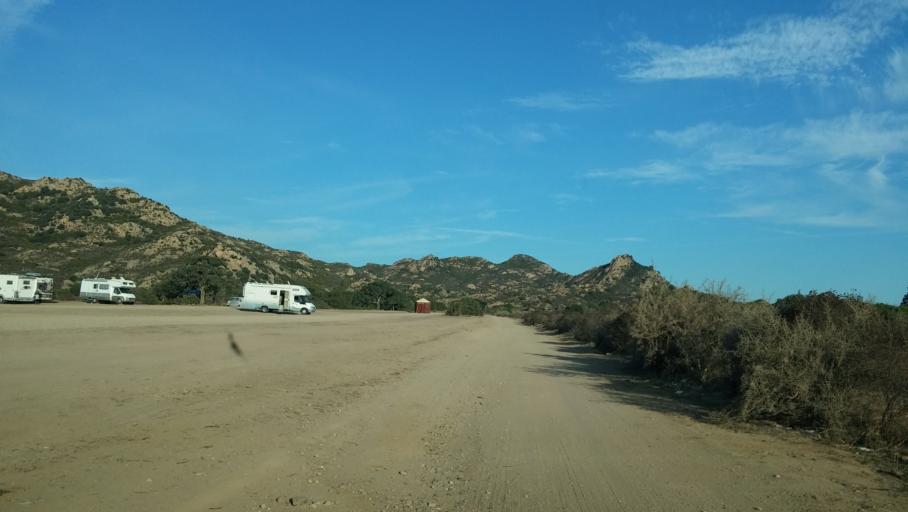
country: IT
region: Sardinia
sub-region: Provincia di Nuoro
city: La Caletta
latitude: 40.4804
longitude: 9.8080
